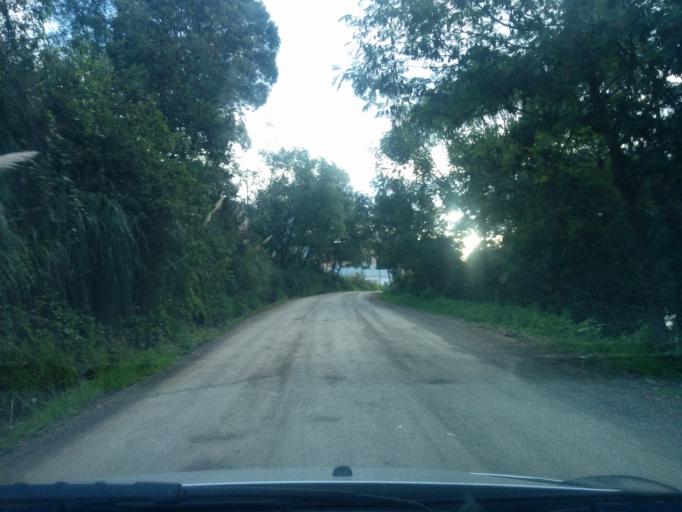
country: EC
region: Azuay
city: Cuenca
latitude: -2.8917
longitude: -78.9585
